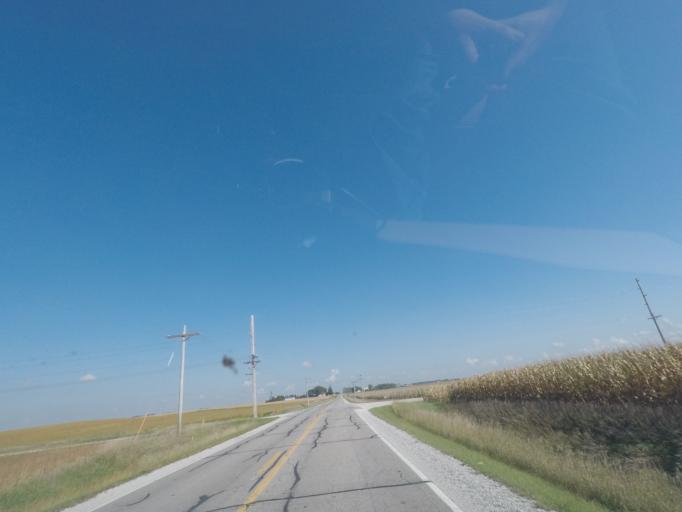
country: US
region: Iowa
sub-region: Story County
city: Nevada
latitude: 42.0340
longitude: -93.4058
